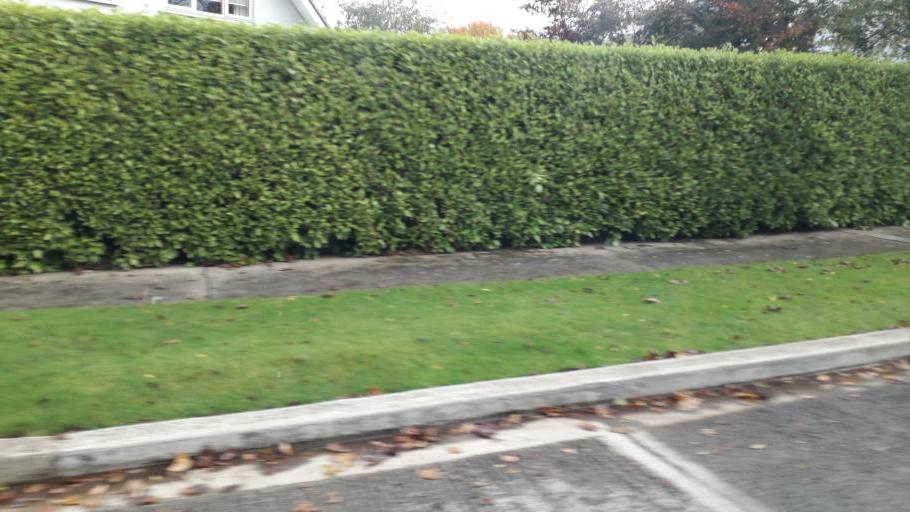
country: IE
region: Leinster
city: Mount Merrion
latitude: 53.2980
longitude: -6.2290
